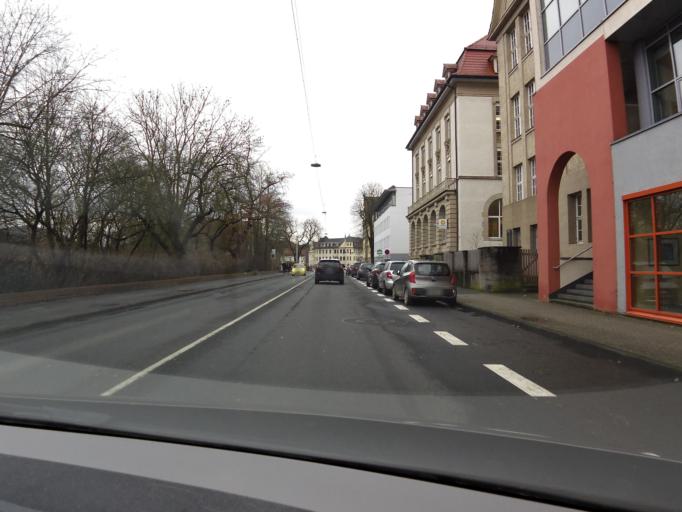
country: DE
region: Hesse
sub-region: Regierungsbezirk Kassel
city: Eschwege
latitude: 51.1897
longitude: 10.0506
